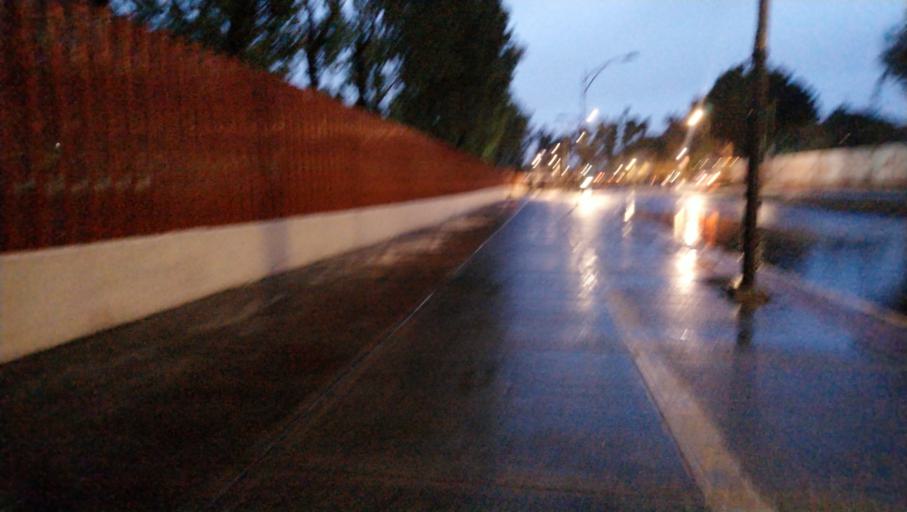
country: MX
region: Mexico City
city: Mexico City
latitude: 19.4319
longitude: -99.1177
